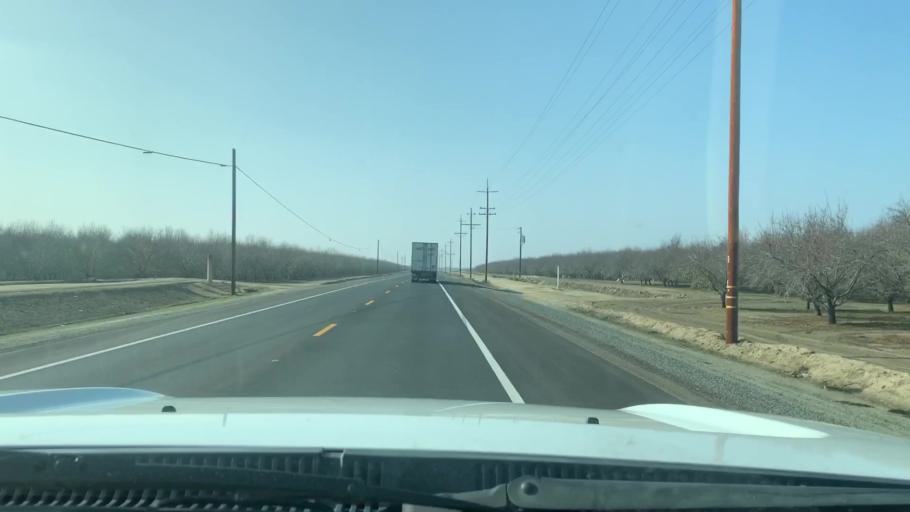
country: US
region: California
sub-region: Kern County
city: Wasco
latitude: 35.6017
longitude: -119.2880
